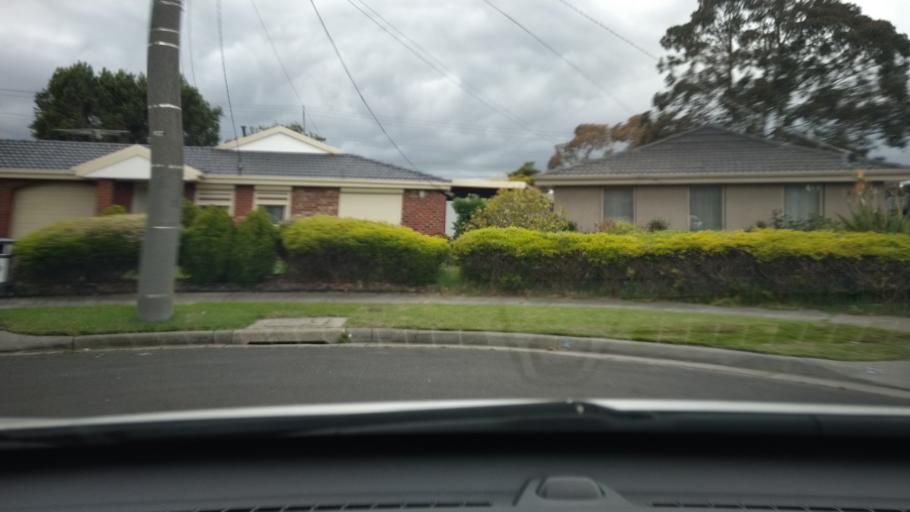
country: AU
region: Victoria
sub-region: Greater Dandenong
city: Keysborough
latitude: -37.9825
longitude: 145.1641
